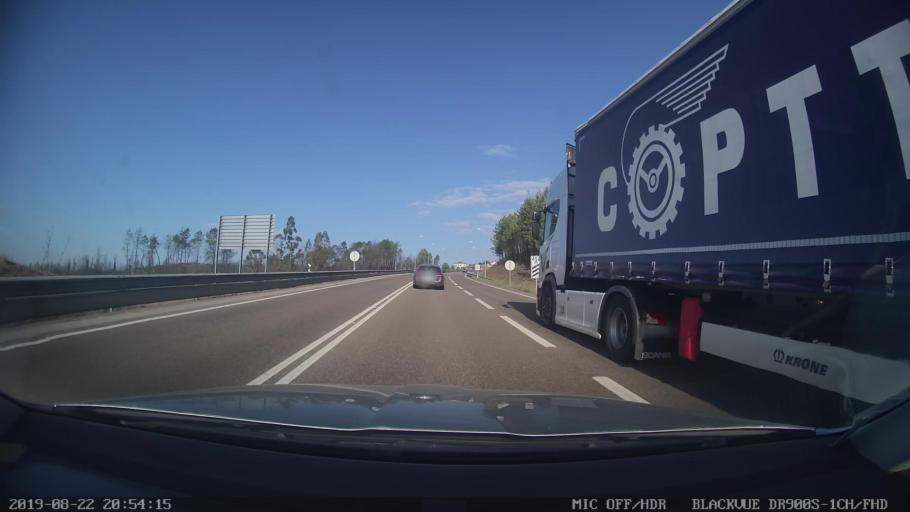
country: PT
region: Castelo Branco
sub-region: Proenca-A-Nova
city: Proenca-a-Nova
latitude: 39.7727
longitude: -8.0100
